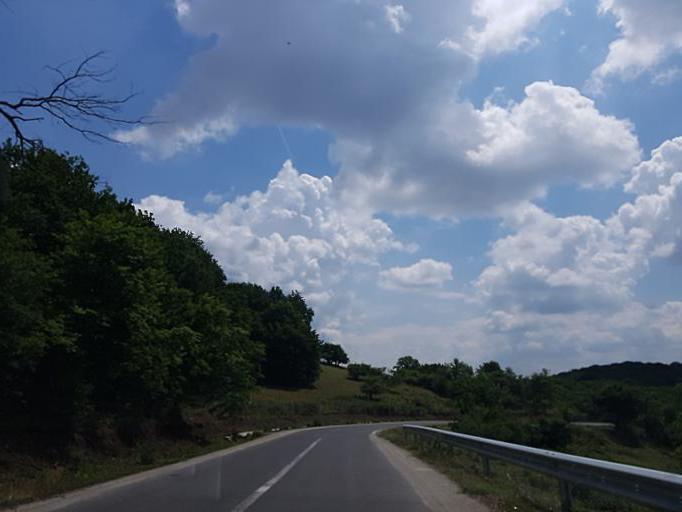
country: RO
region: Sibiu
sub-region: Comuna Seica Mica
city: Seica Mica
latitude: 46.0428
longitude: 24.1556
